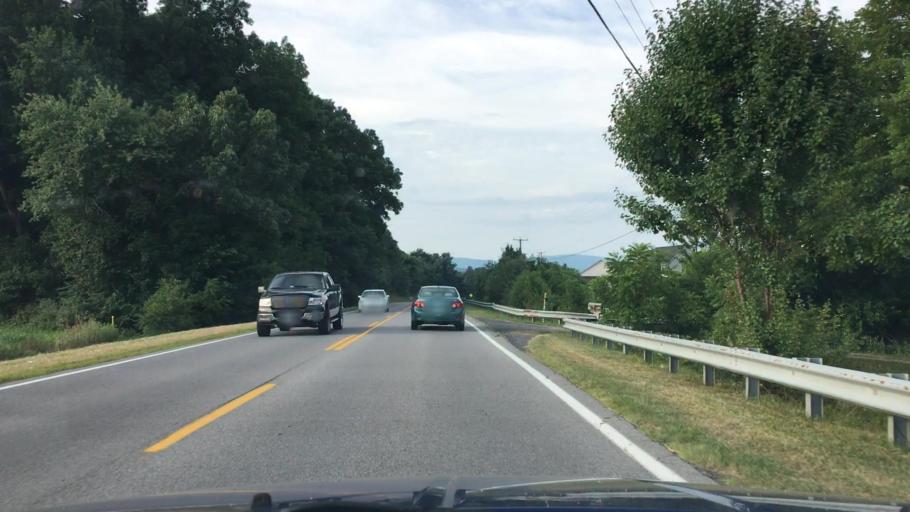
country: US
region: Virginia
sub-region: City of Waynesboro
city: Waynesboro
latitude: 38.0942
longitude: -78.8990
